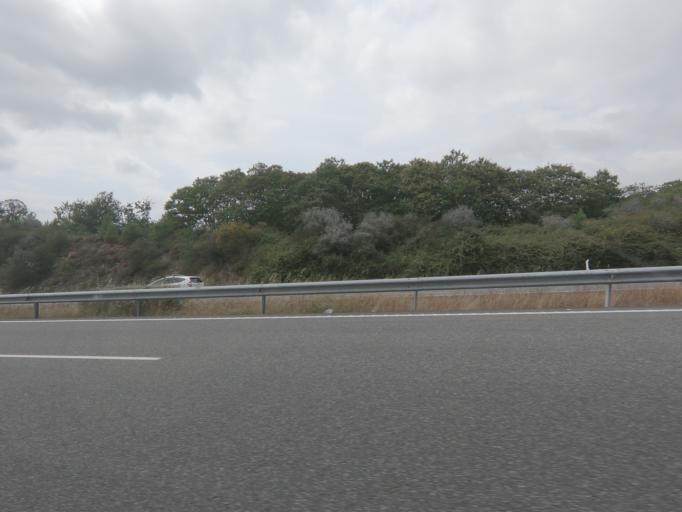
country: ES
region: Galicia
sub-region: Provincia de Pontevedra
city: Ponteareas
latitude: 42.1472
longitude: -8.4450
